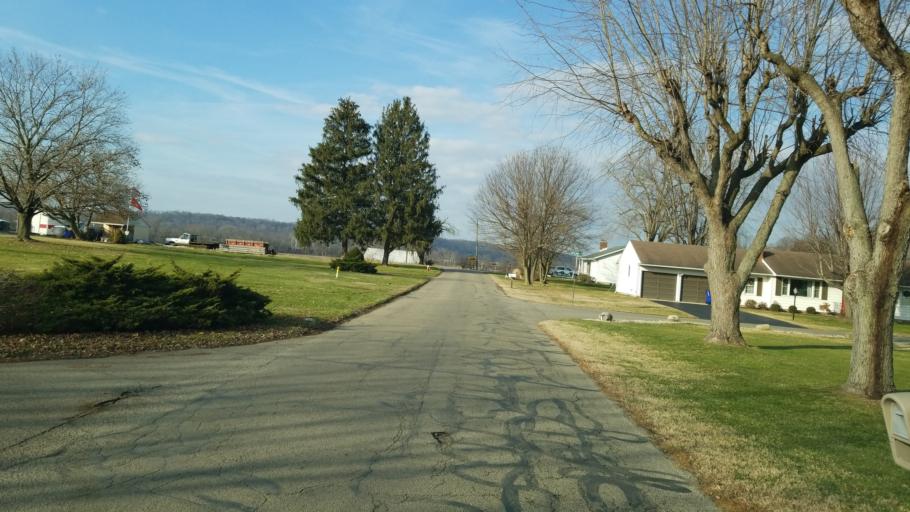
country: US
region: Ohio
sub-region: Ross County
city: Chillicothe
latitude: 39.3566
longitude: -82.9825
